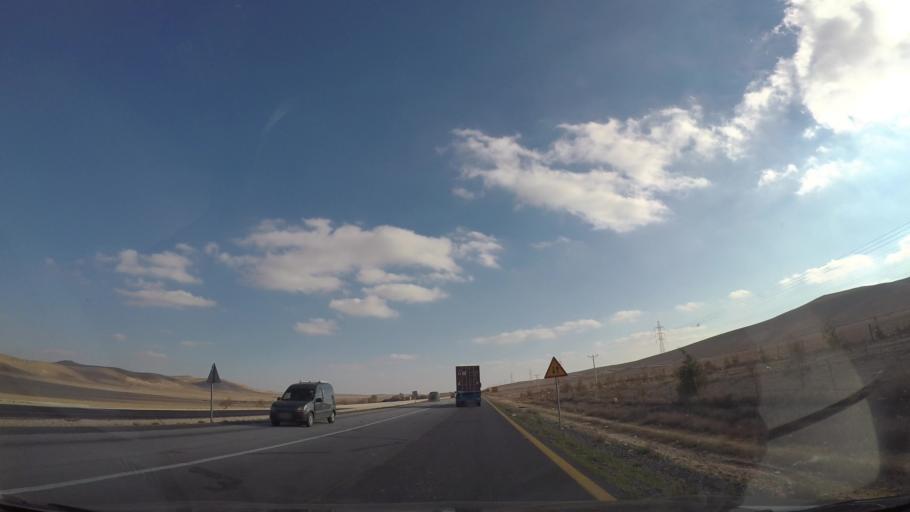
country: JO
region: Karak
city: Karak City
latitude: 31.1847
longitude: 36.0187
